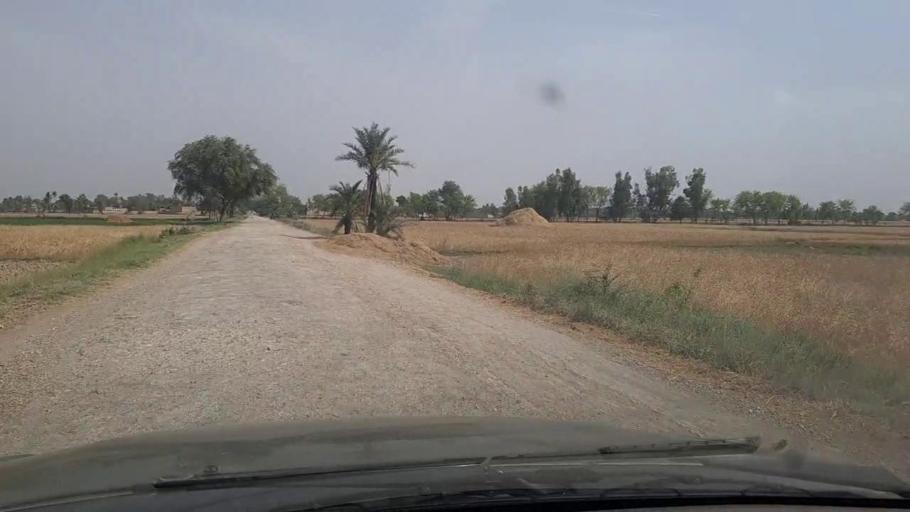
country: PK
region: Sindh
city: Chak
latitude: 27.8344
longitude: 68.7705
